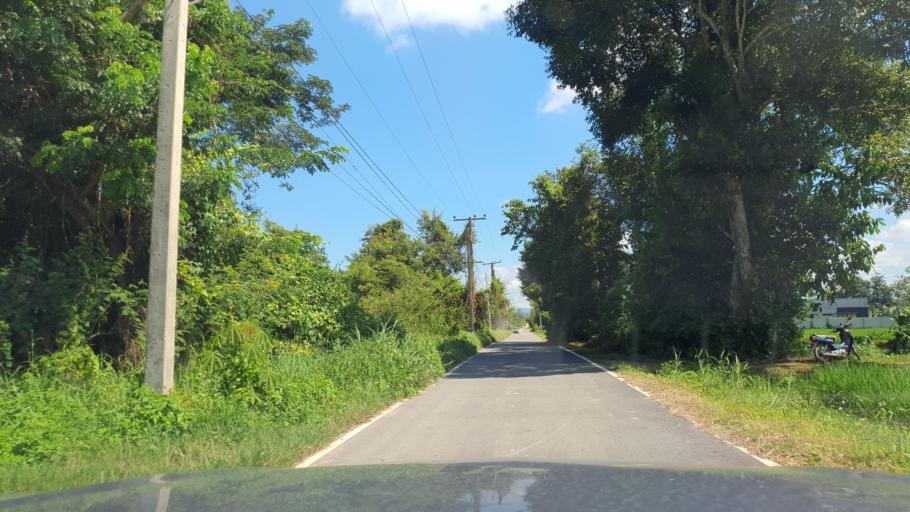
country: TH
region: Chiang Mai
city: San Kamphaeng
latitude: 18.7684
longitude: 99.1694
